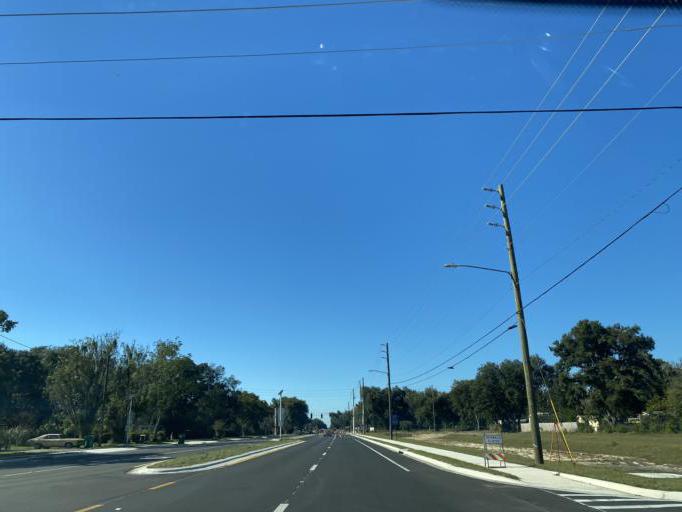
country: US
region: Florida
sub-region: Lake County
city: Fruitland Park
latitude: 28.8616
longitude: -81.9119
